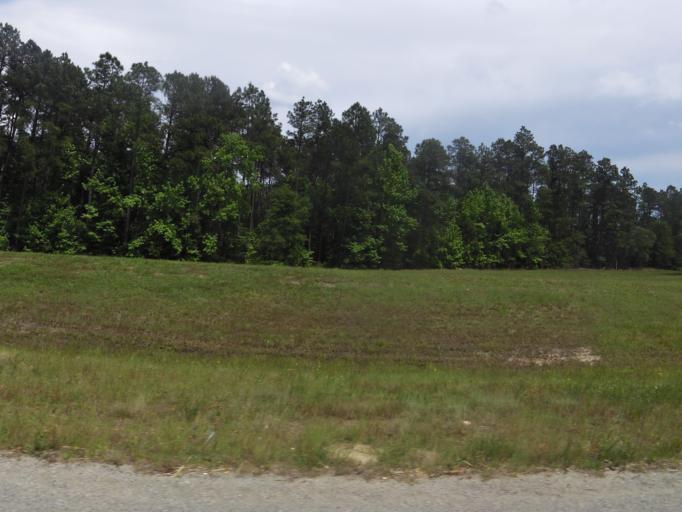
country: US
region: Georgia
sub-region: Emanuel County
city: Swainsboro
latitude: 32.6438
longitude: -82.3659
